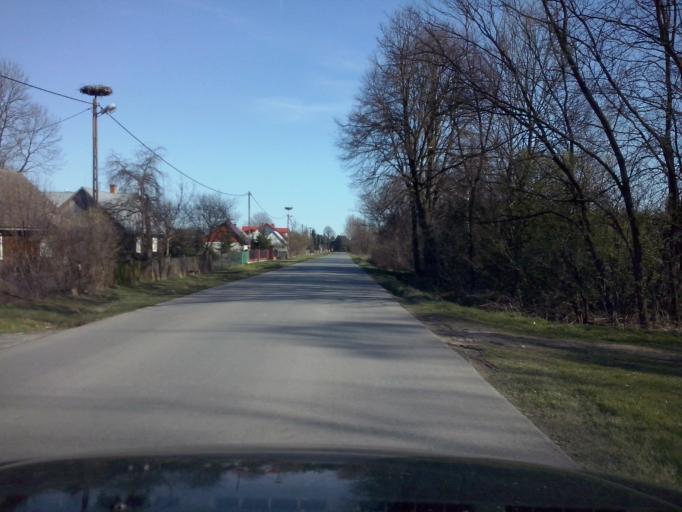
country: PL
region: Subcarpathian Voivodeship
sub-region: Powiat lezajski
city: Kurylowka
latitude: 50.3400
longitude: 22.4369
